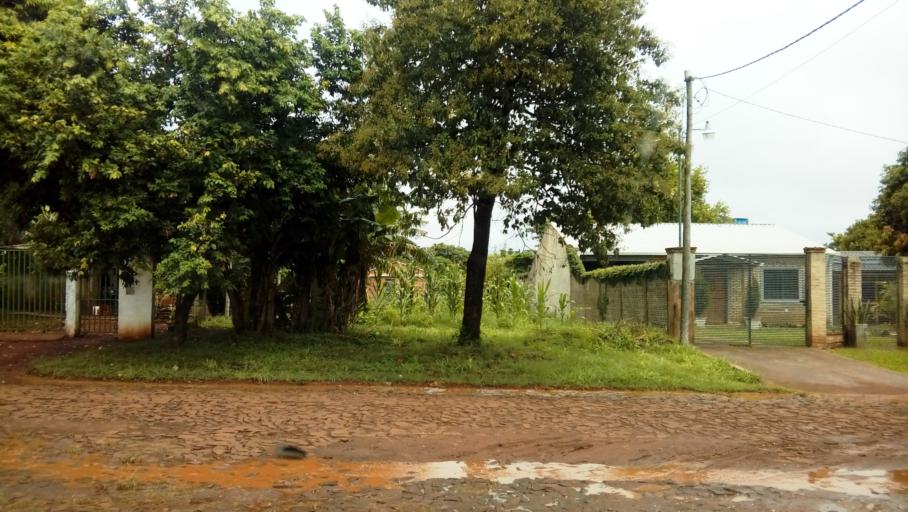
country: PY
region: Alto Parana
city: Ciudad del Este
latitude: -25.4213
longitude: -54.6443
